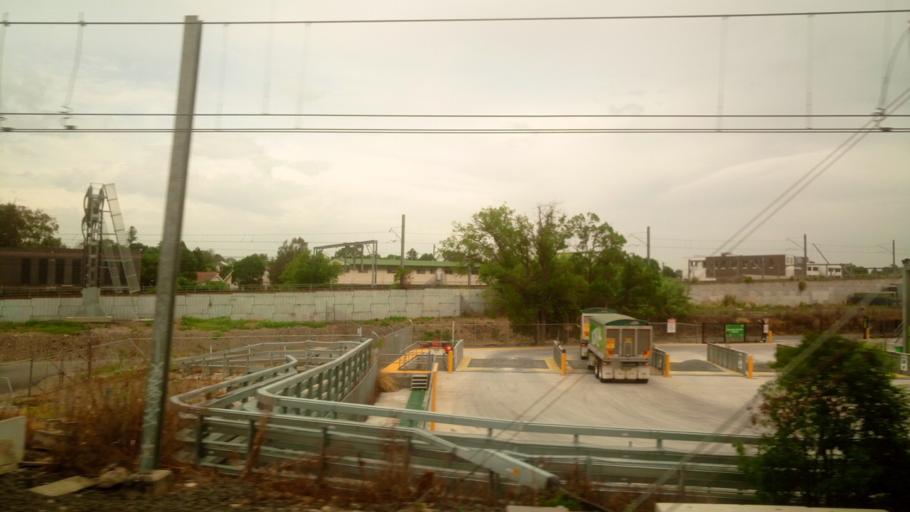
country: AU
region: New South Wales
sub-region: Parramatta
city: Harris Park
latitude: -33.8296
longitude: 151.0084
